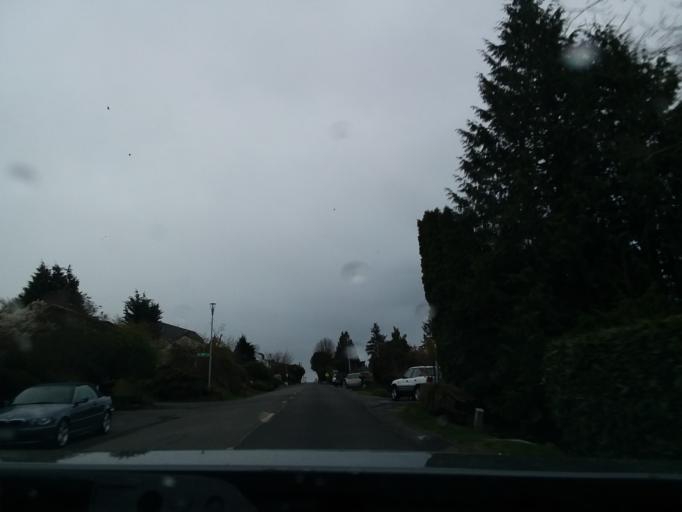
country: US
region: Washington
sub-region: King County
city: Shoreline
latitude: 47.7000
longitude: -122.3876
